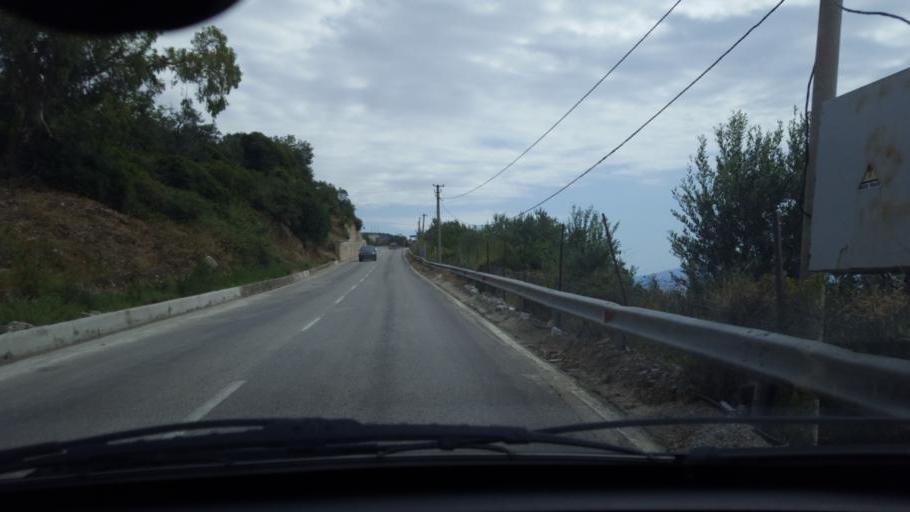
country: AL
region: Vlore
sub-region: Rrethi i Sarandes
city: Lukove
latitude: 40.0598
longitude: 19.8587
